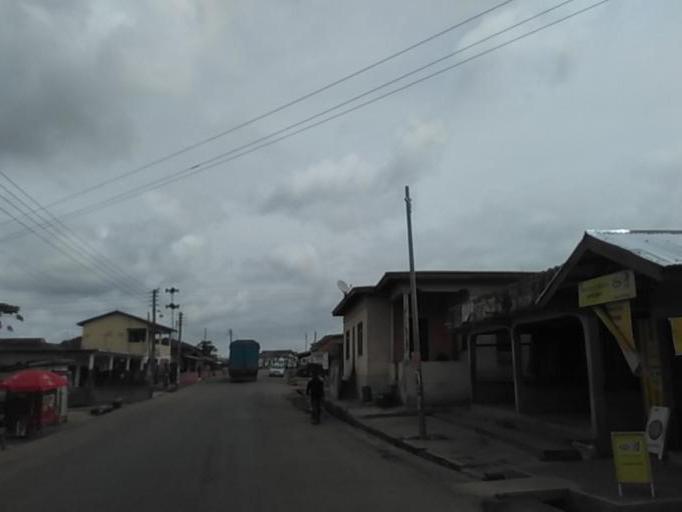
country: GH
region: Ashanti
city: Mamponteng
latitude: 6.7911
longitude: -1.4712
